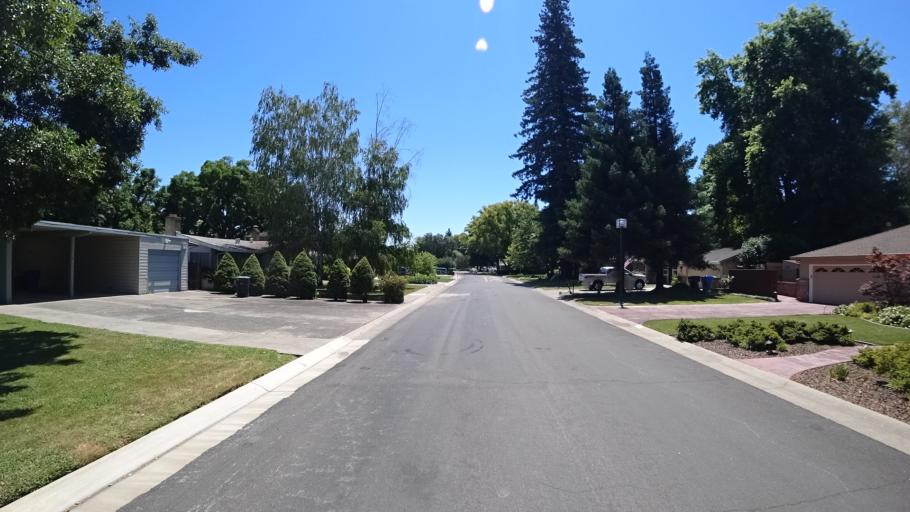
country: US
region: California
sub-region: Yolo County
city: West Sacramento
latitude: 38.5319
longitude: -121.5205
